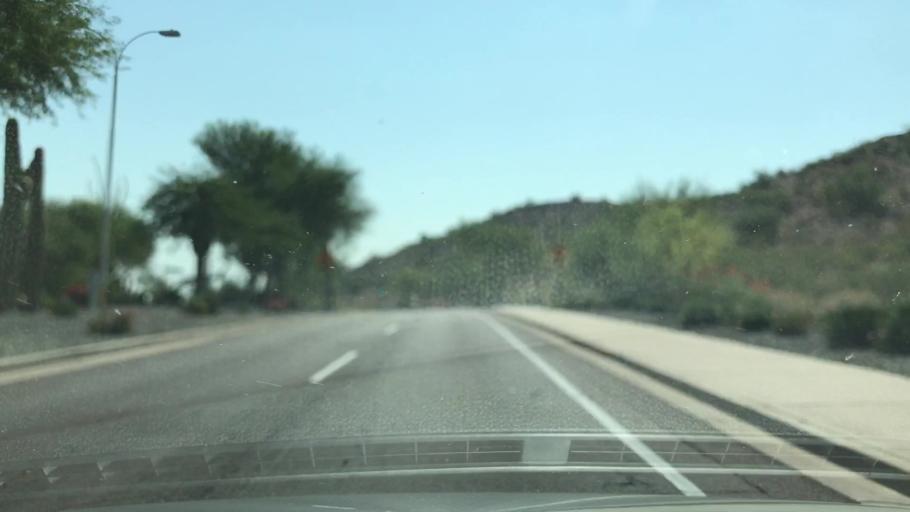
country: US
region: Arizona
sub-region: Maricopa County
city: Guadalupe
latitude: 33.3047
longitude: -112.0354
